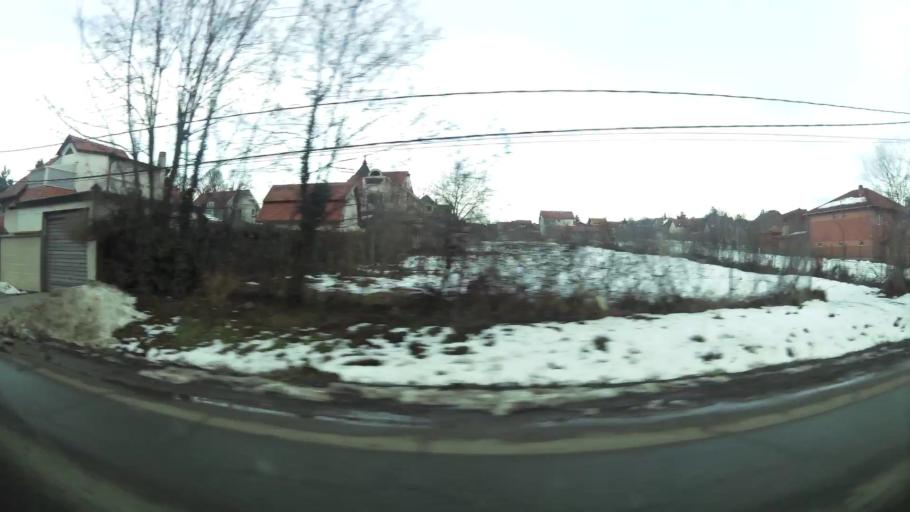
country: RS
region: Central Serbia
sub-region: Belgrade
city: Vozdovac
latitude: 44.7477
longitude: 20.4768
